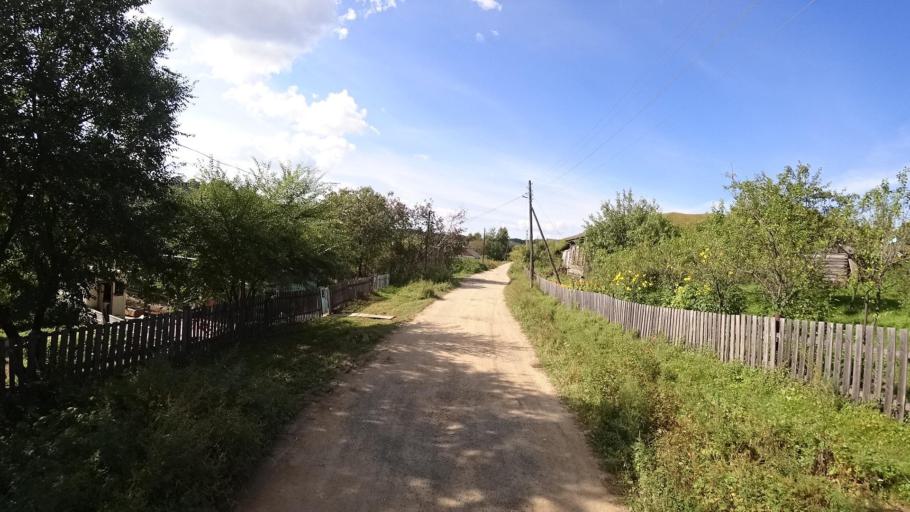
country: RU
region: Jewish Autonomous Oblast
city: Birakan
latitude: 48.9976
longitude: 131.7225
